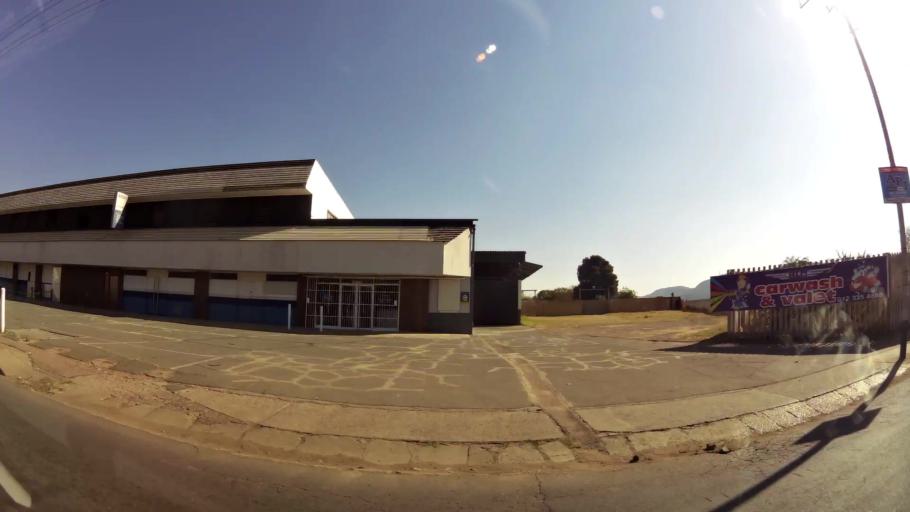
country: ZA
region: Gauteng
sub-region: City of Tshwane Metropolitan Municipality
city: Pretoria
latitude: -25.7063
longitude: 28.2005
